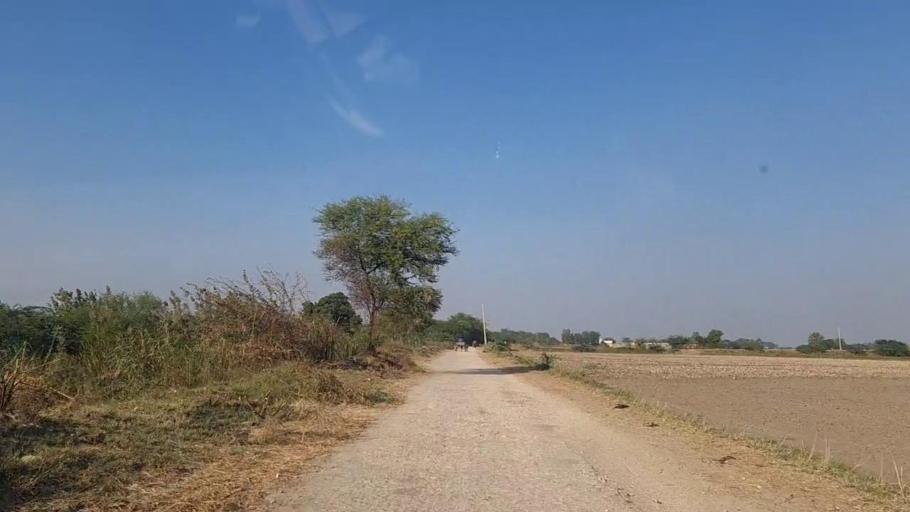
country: PK
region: Sindh
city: Thatta
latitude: 24.7544
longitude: 67.9611
